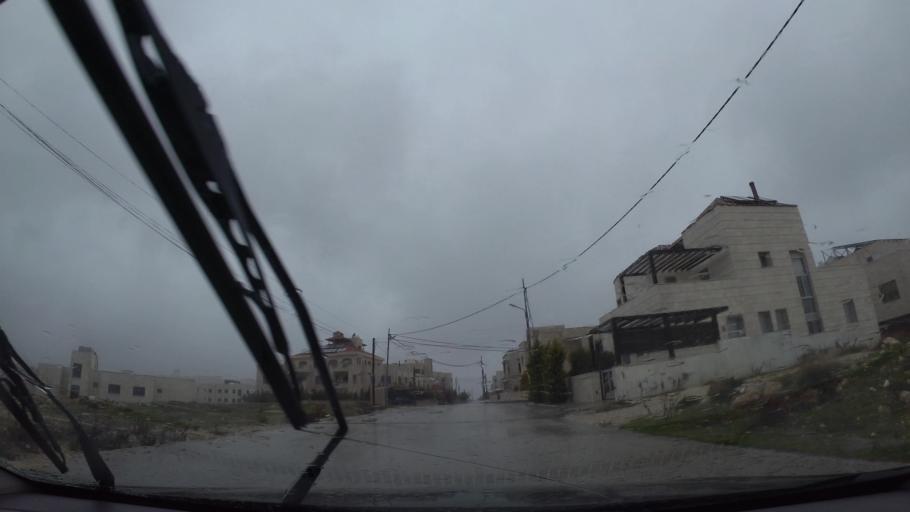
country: JO
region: Amman
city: Al Jubayhah
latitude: 32.0102
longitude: 35.8967
